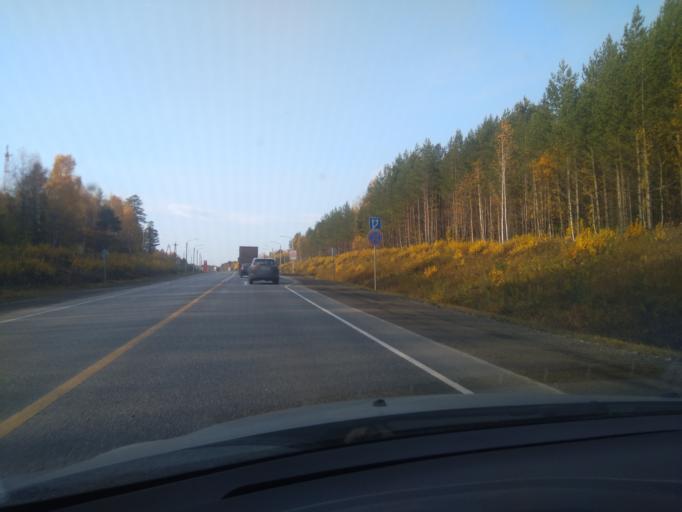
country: RU
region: Sverdlovsk
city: Druzhinino
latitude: 56.8074
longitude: 59.4887
